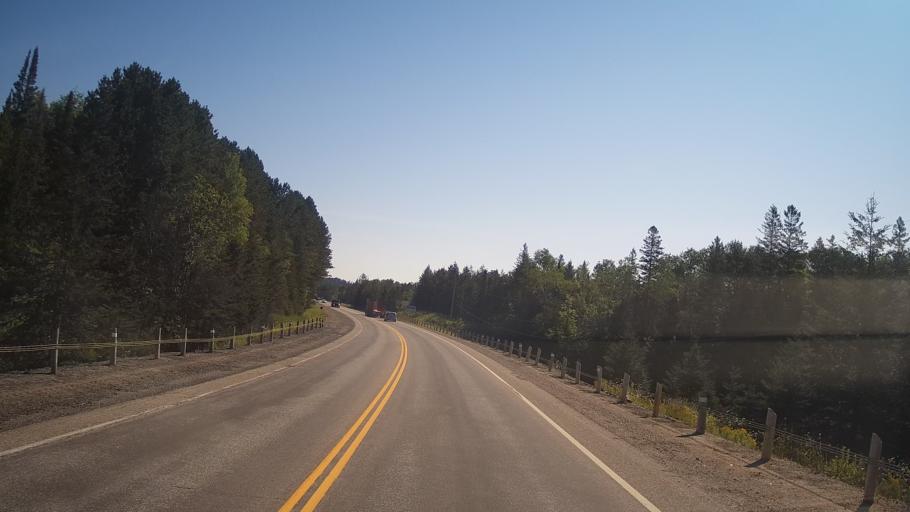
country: CA
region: Ontario
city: Espanola
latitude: 46.2213
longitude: -82.0181
